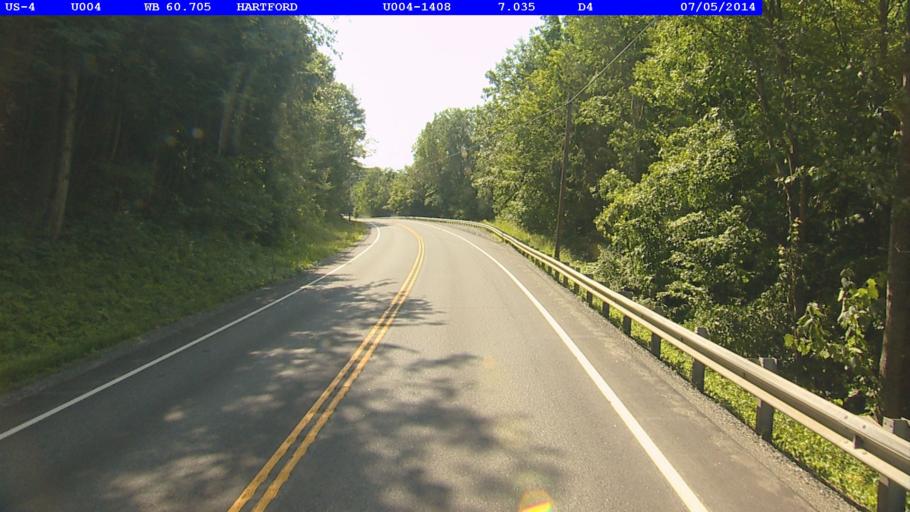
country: US
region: Vermont
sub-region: Windsor County
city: White River Junction
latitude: 43.6643
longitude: -72.3714
